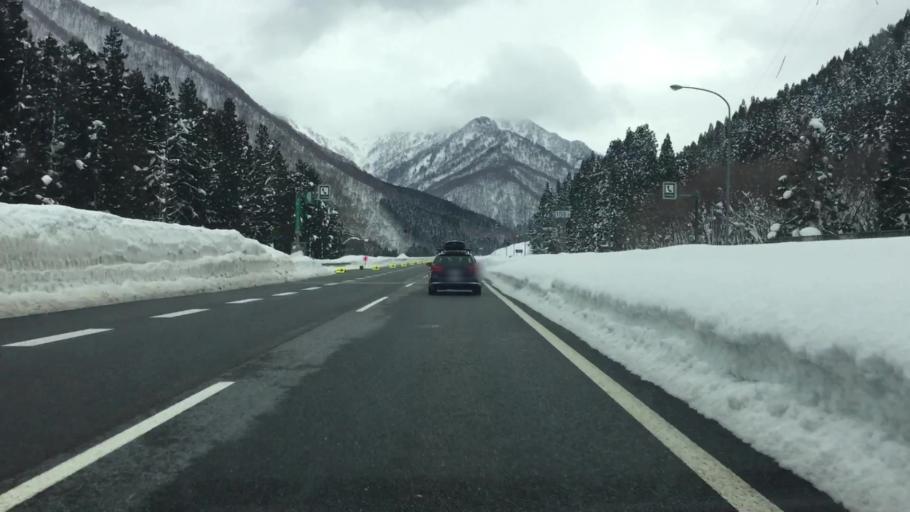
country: JP
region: Niigata
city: Shiozawa
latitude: 36.8798
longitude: 138.8561
